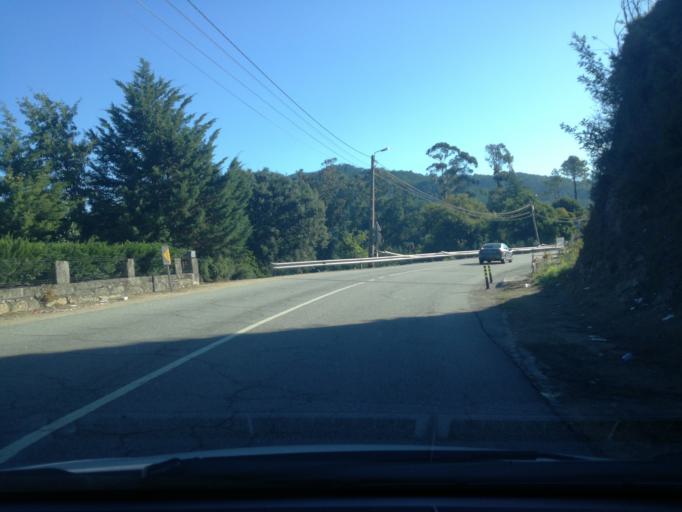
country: PT
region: Braga
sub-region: Vieira do Minho
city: Real
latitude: 41.6792
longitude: -8.1759
